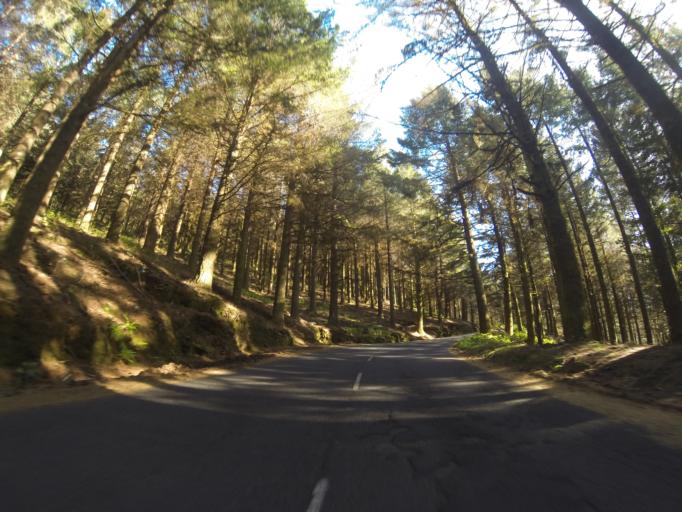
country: PT
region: Madeira
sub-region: Funchal
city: Nossa Senhora do Monte
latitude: 32.7133
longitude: -16.8875
